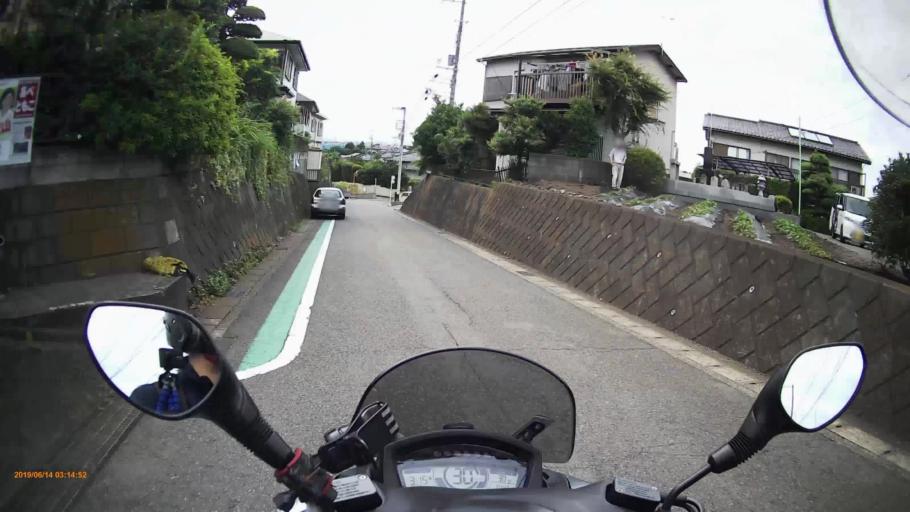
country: JP
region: Kanagawa
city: Fujisawa
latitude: 35.4125
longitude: 139.4594
